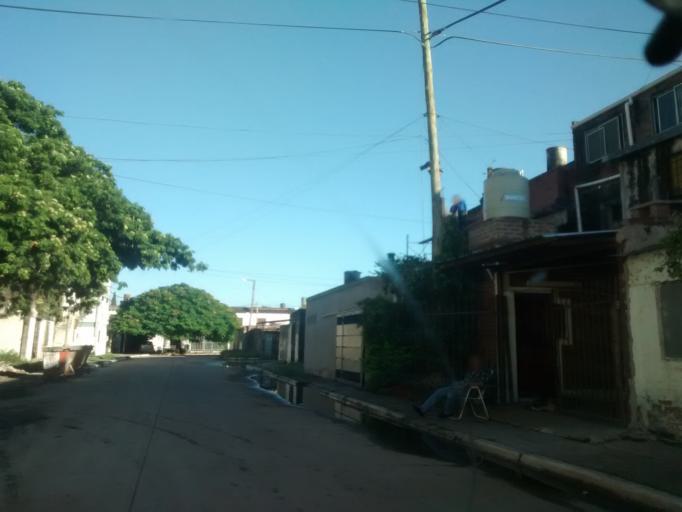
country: AR
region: Chaco
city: Fontana
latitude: -27.4479
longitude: -59.0169
